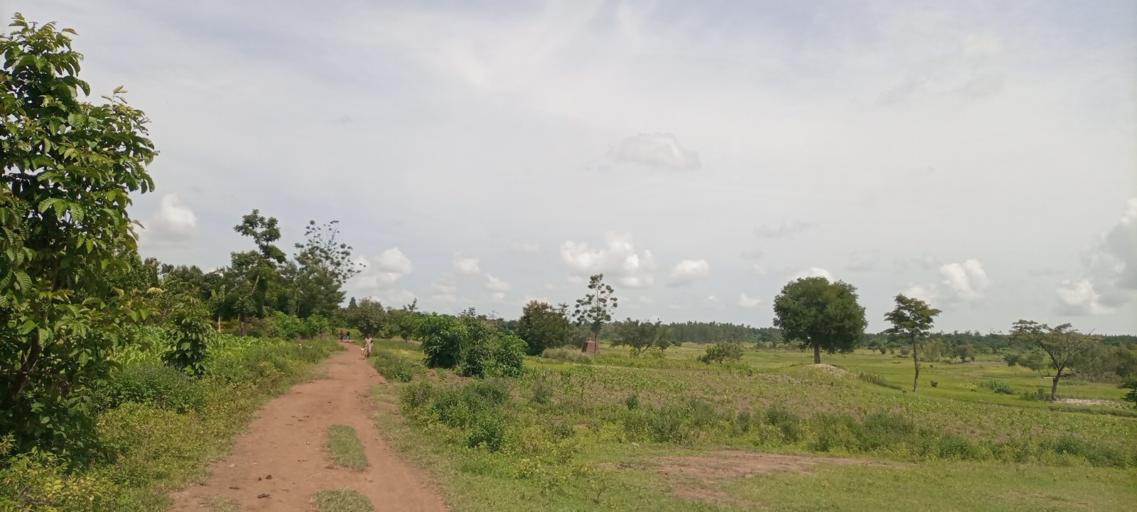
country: UG
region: Eastern Region
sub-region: Budaka District
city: Budaka
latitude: 1.1731
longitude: 33.9528
